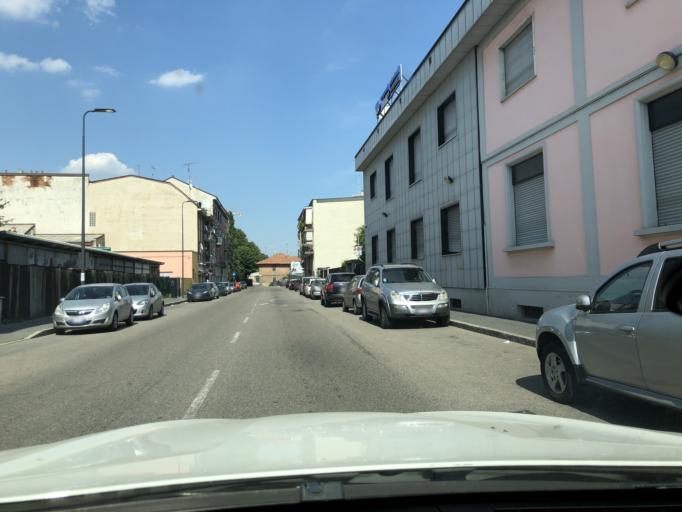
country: IT
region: Lombardy
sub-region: Citta metropolitana di Milano
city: Novate Milanese
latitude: 45.5122
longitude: 9.1565
